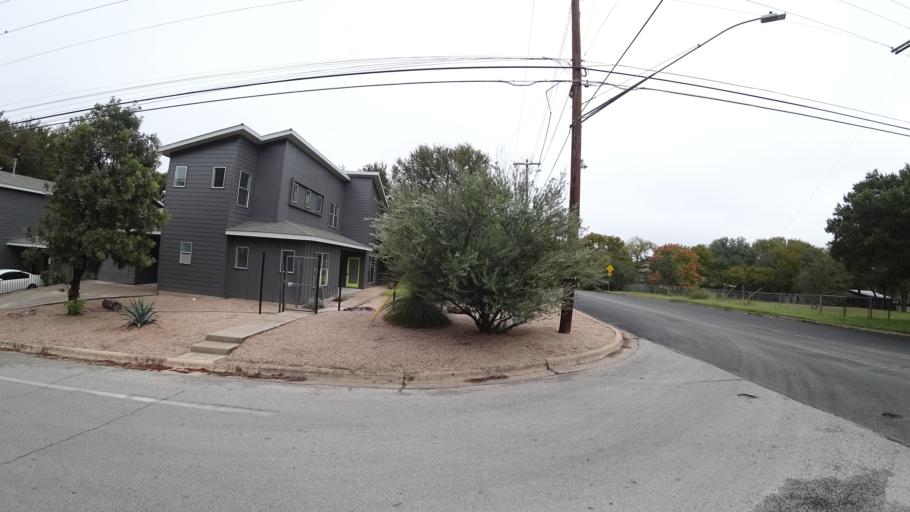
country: US
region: Texas
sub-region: Travis County
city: Rollingwood
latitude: 30.2529
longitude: -97.7786
